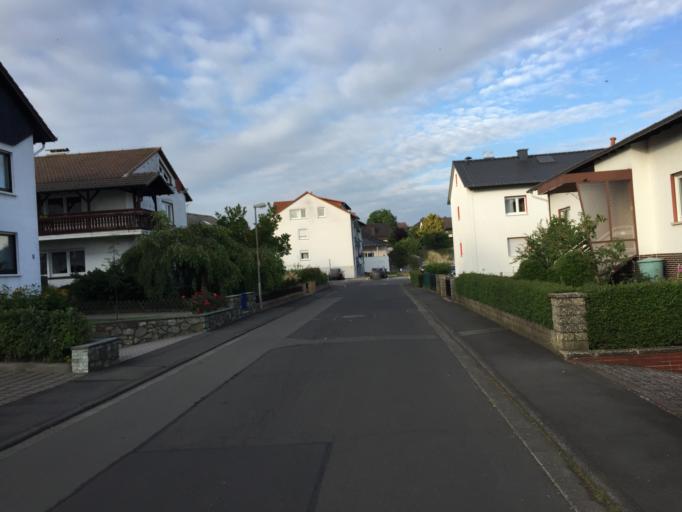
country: DE
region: Hesse
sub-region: Regierungsbezirk Giessen
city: Reiskirchen
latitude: 50.6007
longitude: 8.8283
